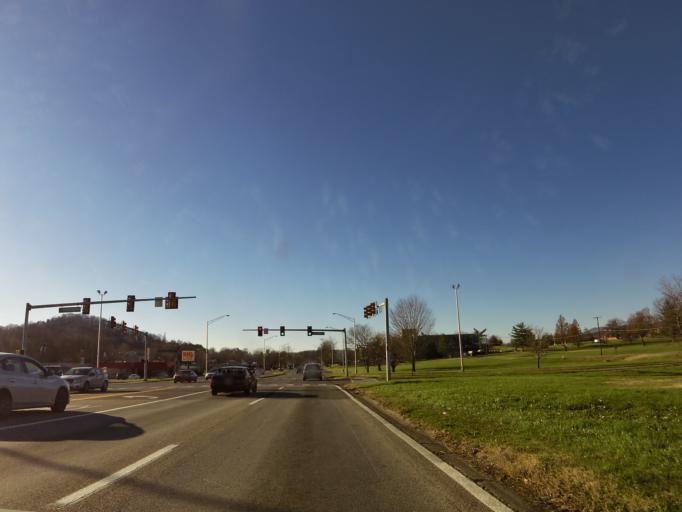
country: US
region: Tennessee
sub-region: Anderson County
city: Oak Ridge
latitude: 36.0070
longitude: -84.2570
